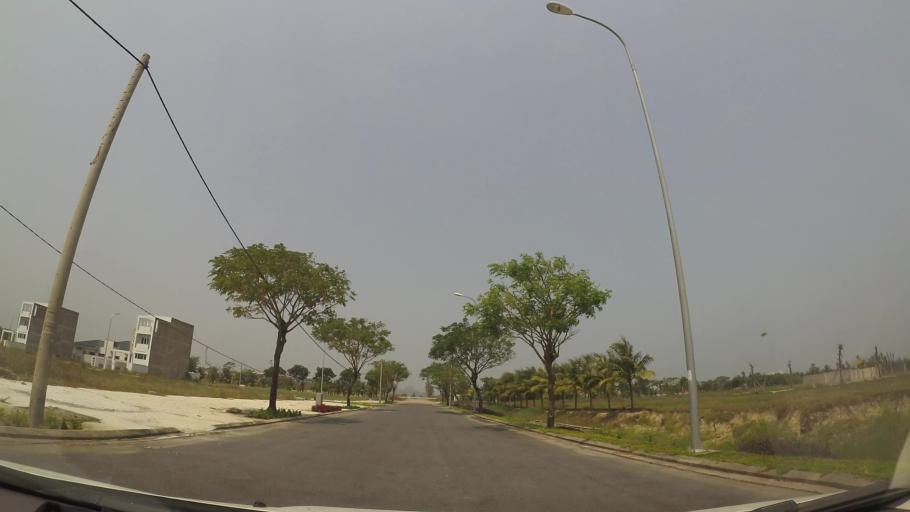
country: VN
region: Da Nang
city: Ngu Hanh Son
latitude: 15.9721
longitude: 108.2644
